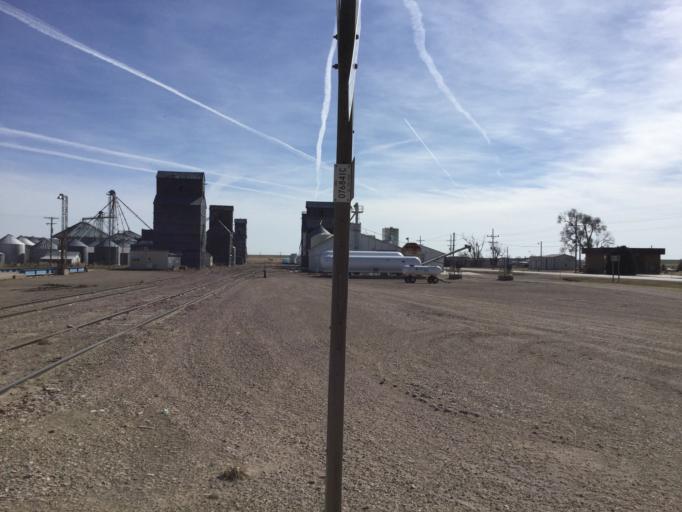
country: US
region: Kansas
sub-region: Cheyenne County
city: Saint Francis
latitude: 39.7569
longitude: -101.5328
